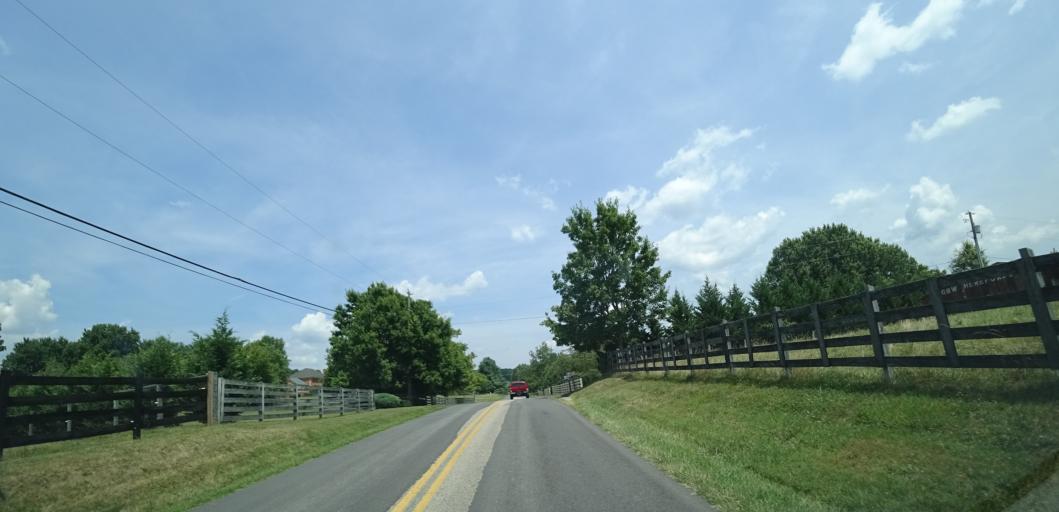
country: US
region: Virginia
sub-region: Botetourt County
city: Fincastle
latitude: 37.4664
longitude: -79.8430
